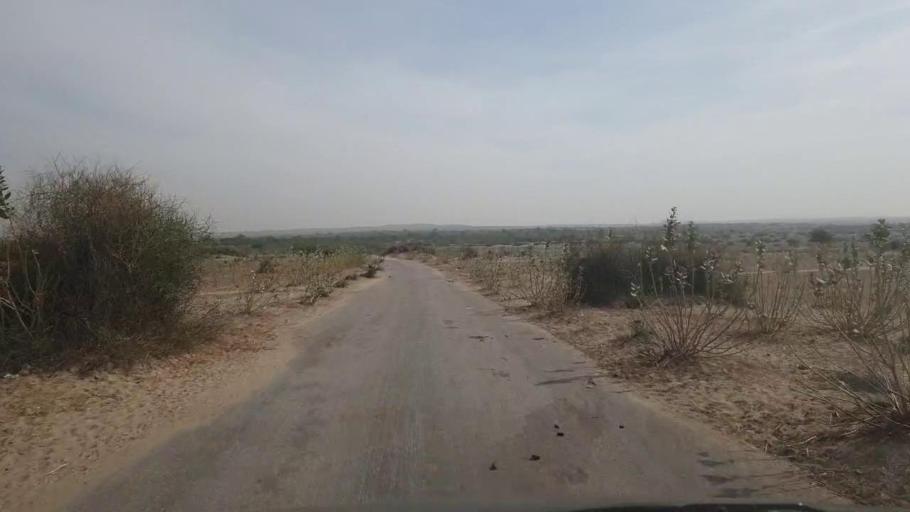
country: PK
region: Sindh
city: Umarkot
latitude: 25.2923
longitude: 69.7249
